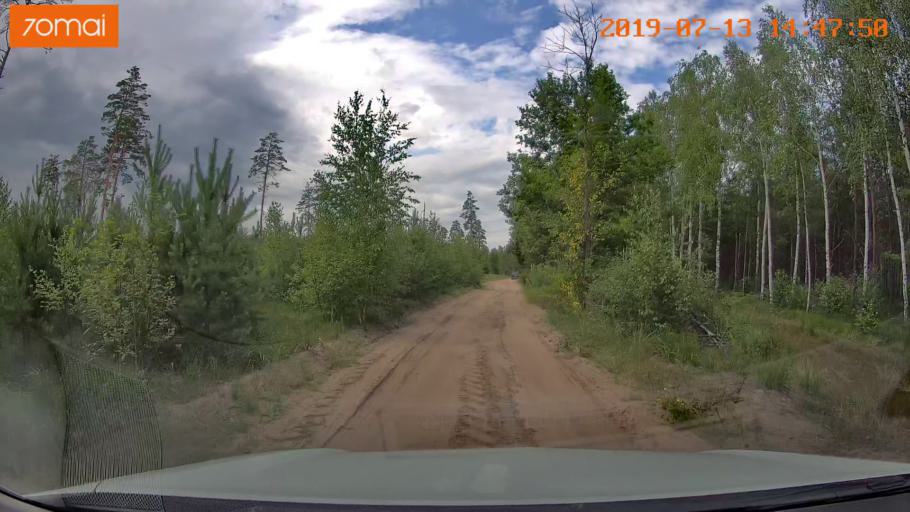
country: BY
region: Mogilev
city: Asipovichy
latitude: 53.2031
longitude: 28.7526
